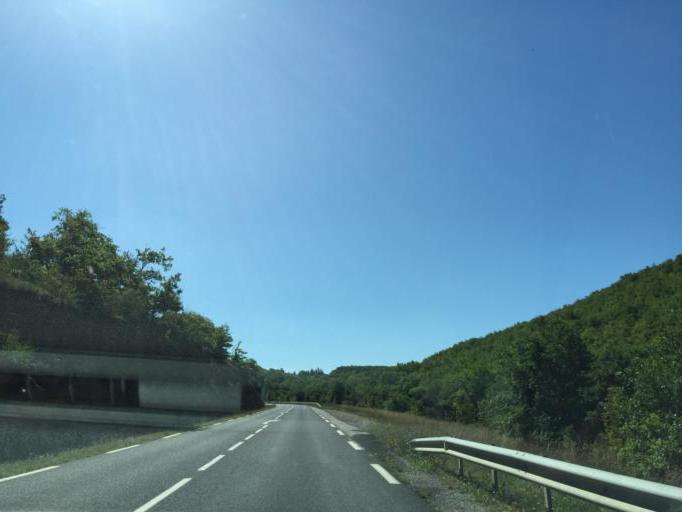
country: FR
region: Midi-Pyrenees
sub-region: Departement de l'Aveyron
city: Saint-Georges-de-Luzencon
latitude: 44.0272
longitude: 2.9334
